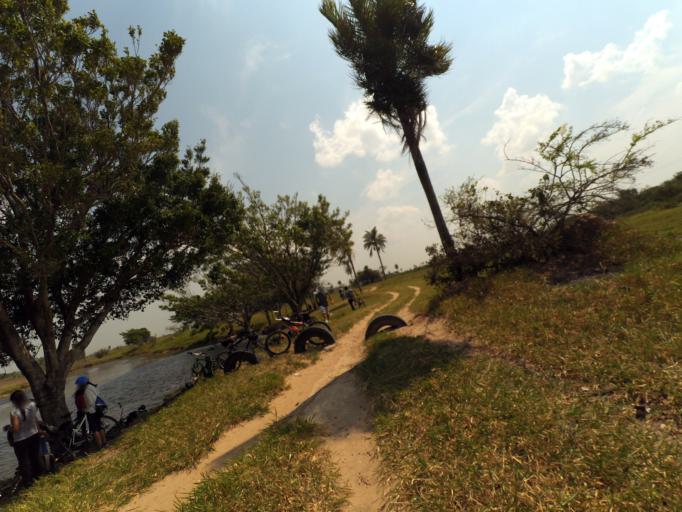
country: BO
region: Santa Cruz
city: Santa Cruz de la Sierra
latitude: -17.8828
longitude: -63.2068
